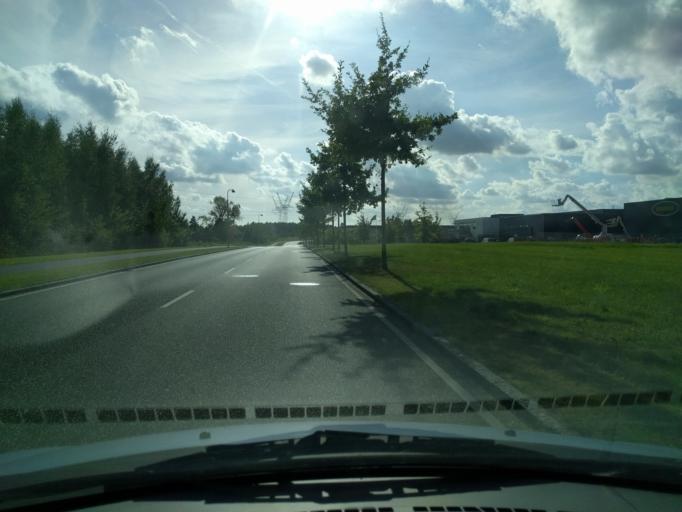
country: DK
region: South Denmark
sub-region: Odense Kommune
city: Neder Holluf
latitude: 55.3660
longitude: 10.5012
